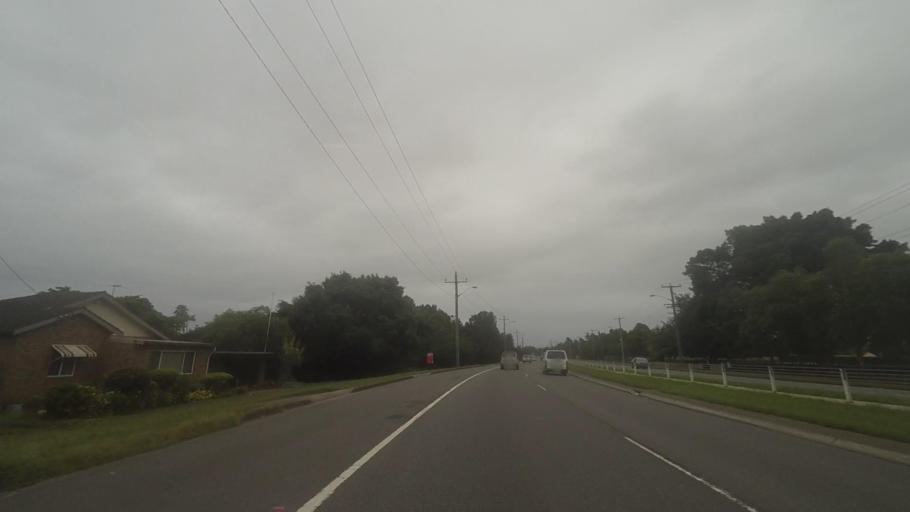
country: AU
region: New South Wales
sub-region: Newcastle
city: Mayfield West
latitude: -32.8655
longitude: 151.7071
